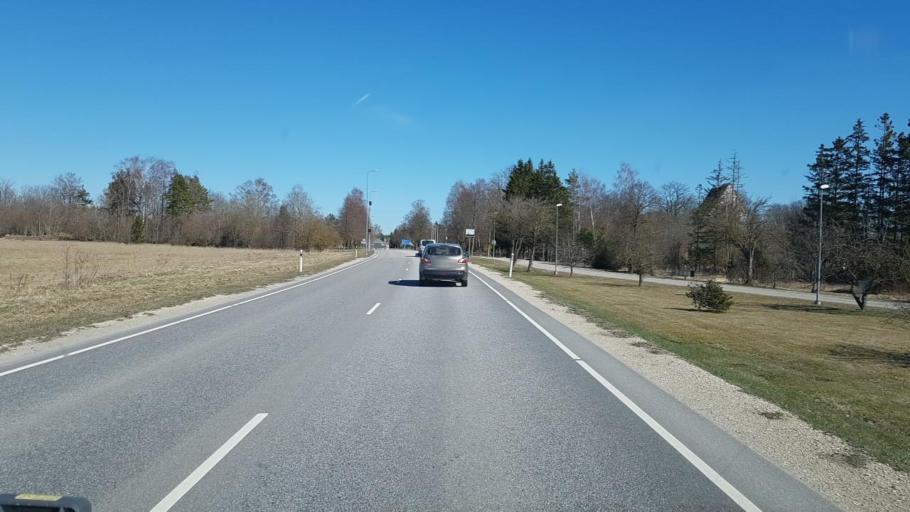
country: EE
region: Saare
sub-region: Orissaare vald
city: Orissaare
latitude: 58.6043
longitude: 23.2216
